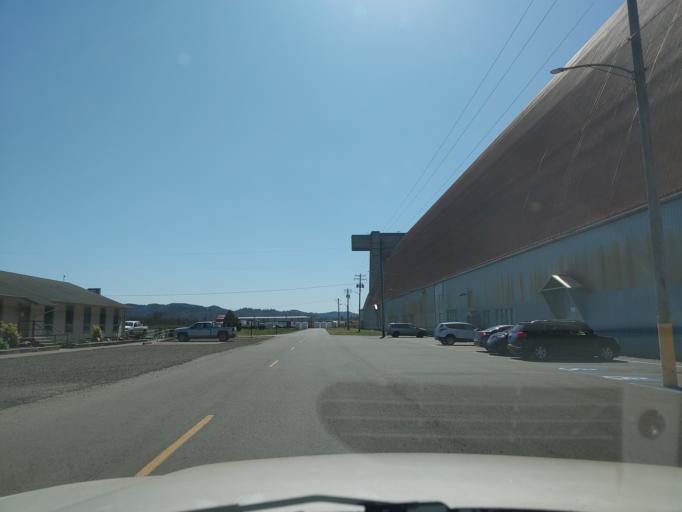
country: US
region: Oregon
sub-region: Tillamook County
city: Tillamook
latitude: 45.4206
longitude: -123.8035
